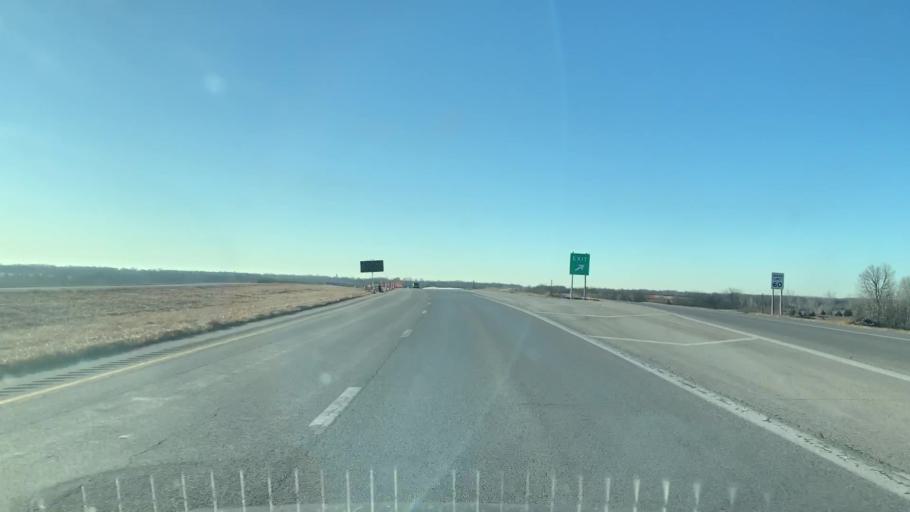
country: US
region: Kansas
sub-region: Bourbon County
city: Fort Scott
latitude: 37.7701
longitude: -94.7061
